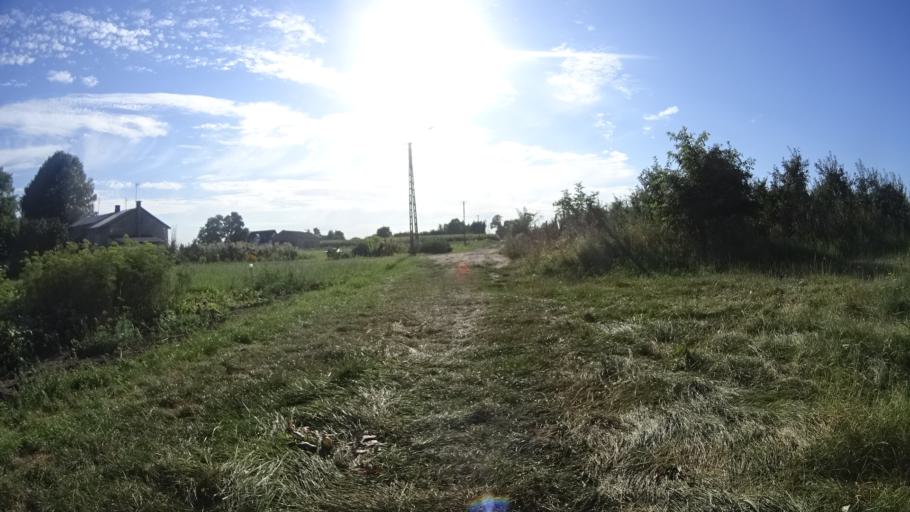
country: PL
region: Masovian Voivodeship
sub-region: Powiat bialobrzeski
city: Wysmierzyce
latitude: 51.6737
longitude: 20.8369
